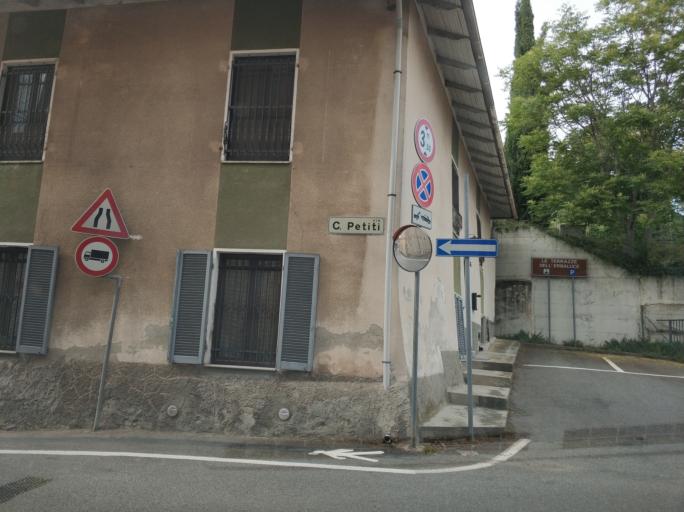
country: IT
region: Piedmont
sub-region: Provincia di Torino
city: Caluso
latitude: 45.3084
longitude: 7.8918
